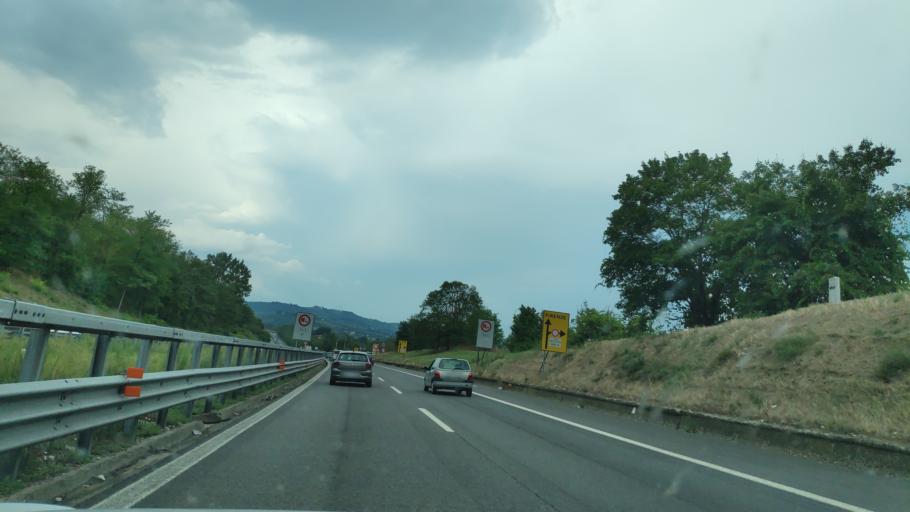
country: IT
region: Tuscany
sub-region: Province of Florence
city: Incisa in Val d'Arno
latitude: 43.6782
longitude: 11.4523
